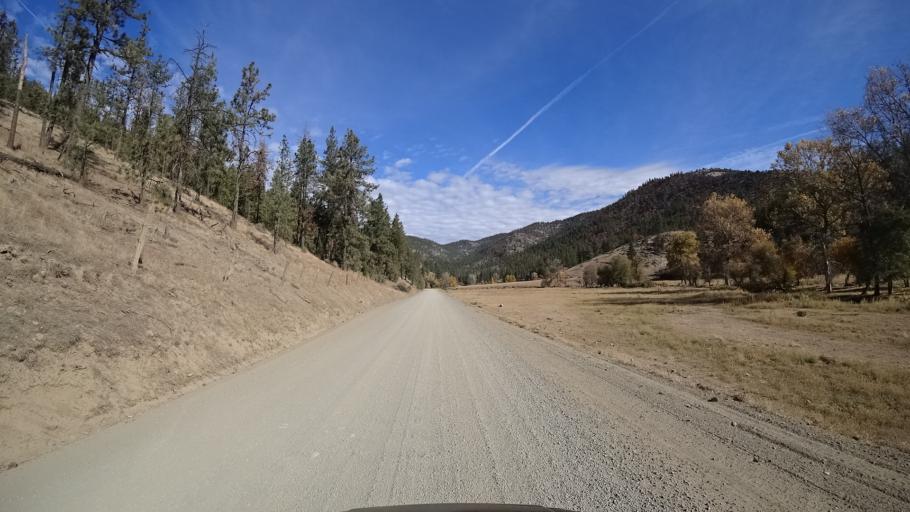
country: US
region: California
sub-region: Siskiyou County
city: Yreka
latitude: 41.6178
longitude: -122.7194
